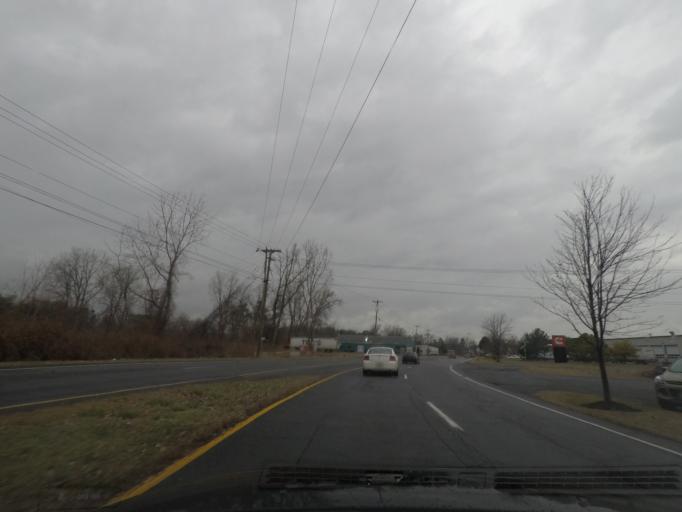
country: US
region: New York
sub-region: Albany County
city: Colonie
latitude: 42.6995
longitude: -73.8291
